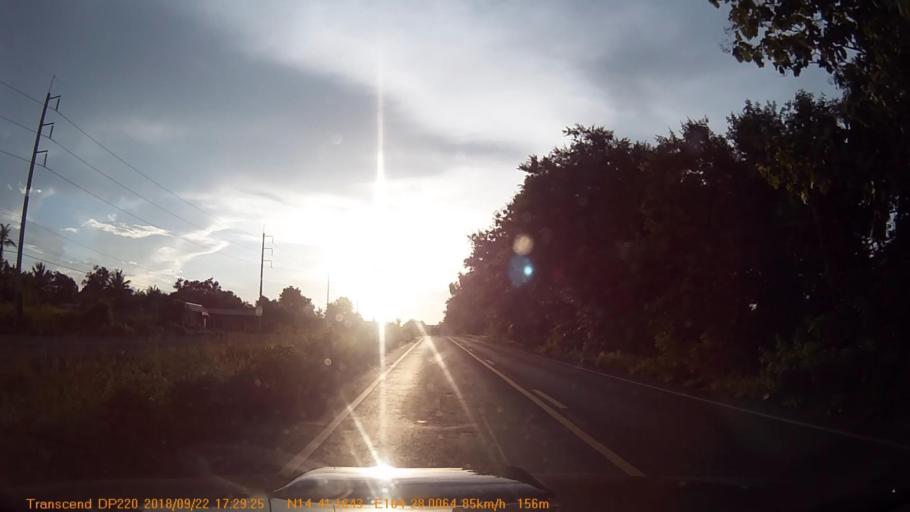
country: TH
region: Sisaket
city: Khun Han
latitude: 14.6861
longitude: 104.4664
